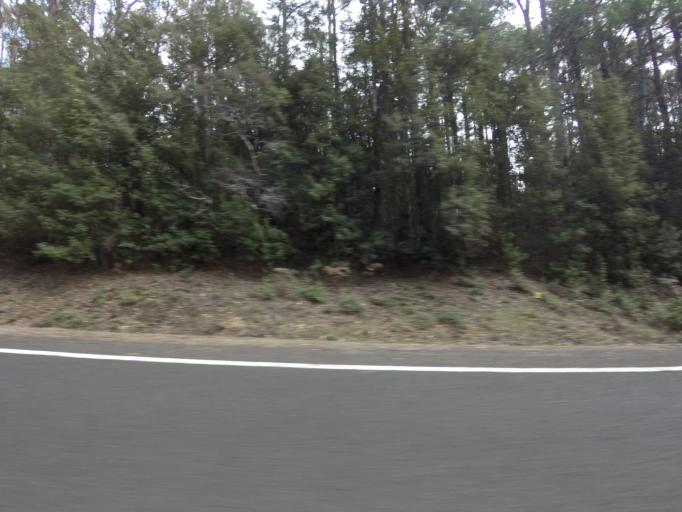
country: AU
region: Tasmania
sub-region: Meander Valley
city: Deloraine
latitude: -41.6434
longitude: 146.7186
